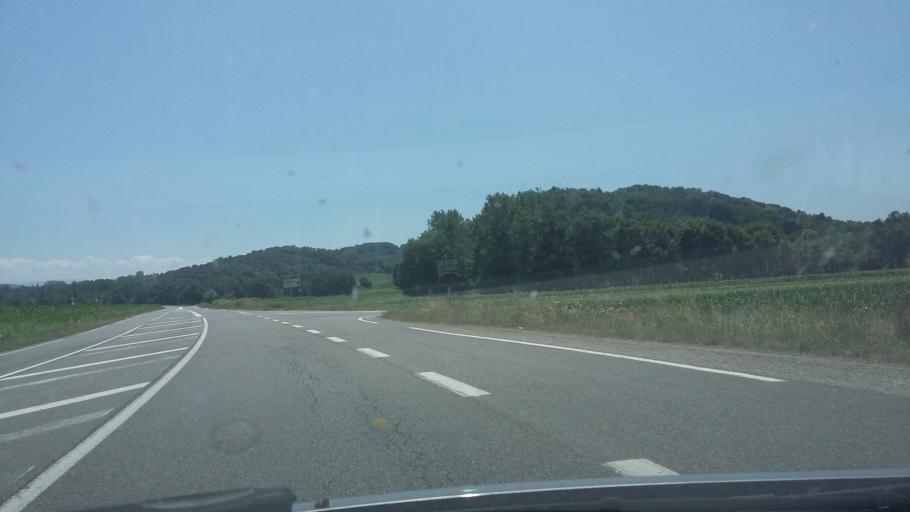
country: FR
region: Rhone-Alpes
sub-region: Departement de l'Ain
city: Belley
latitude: 45.7925
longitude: 5.6827
